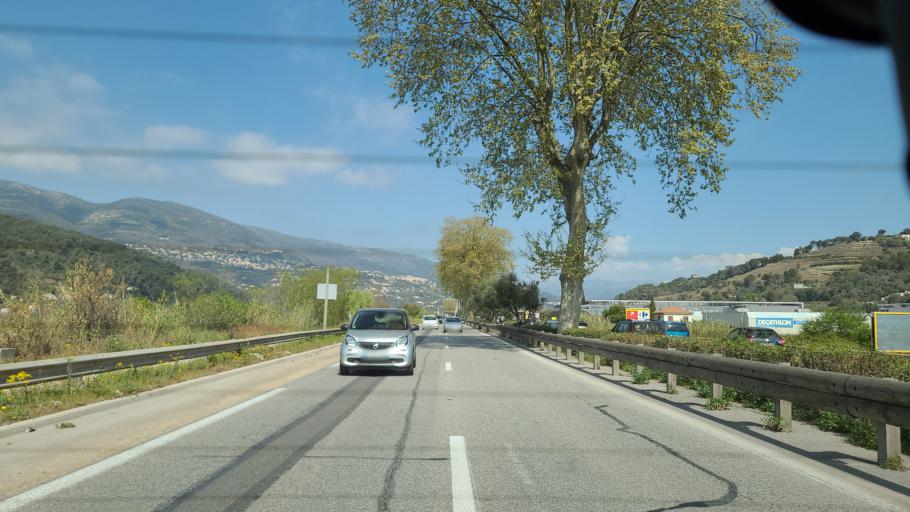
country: FR
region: Provence-Alpes-Cote d'Azur
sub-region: Departement des Alpes-Maritimes
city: La Gaude
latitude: 43.7244
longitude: 7.1857
